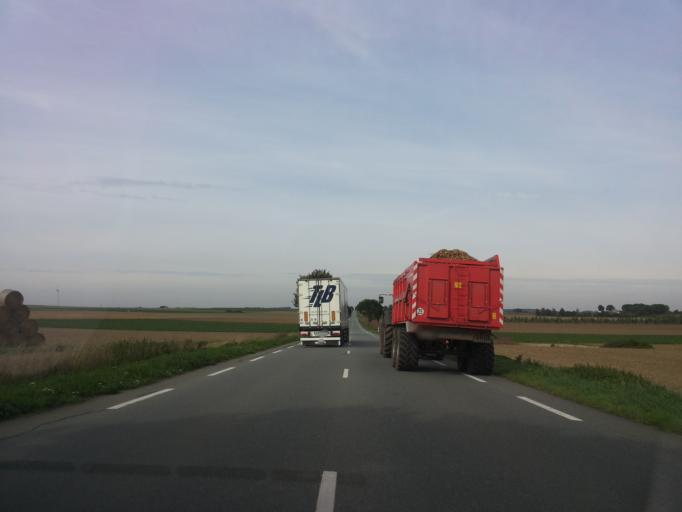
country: FR
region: Nord-Pas-de-Calais
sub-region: Departement du Nord
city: Lecluse
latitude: 50.2391
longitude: 2.9761
